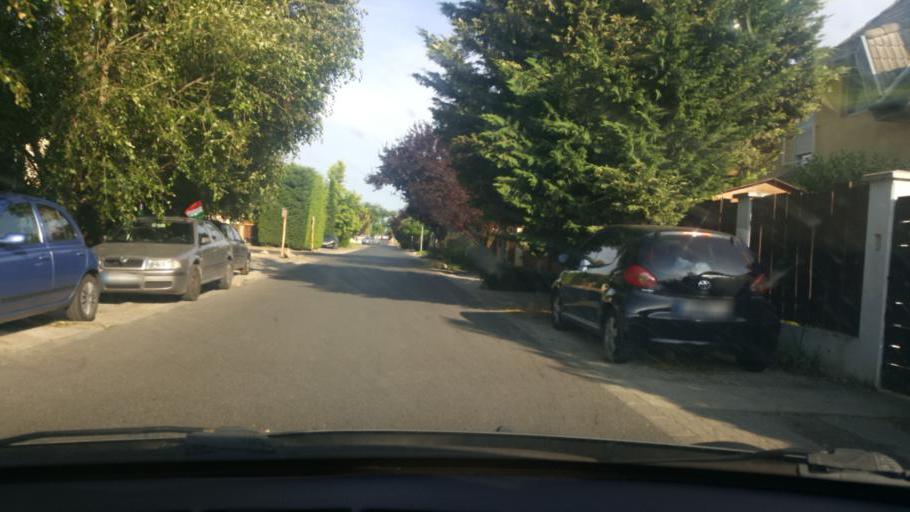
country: HU
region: Budapest
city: Budapest XVII. keruelet
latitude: 47.4685
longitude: 19.2277
